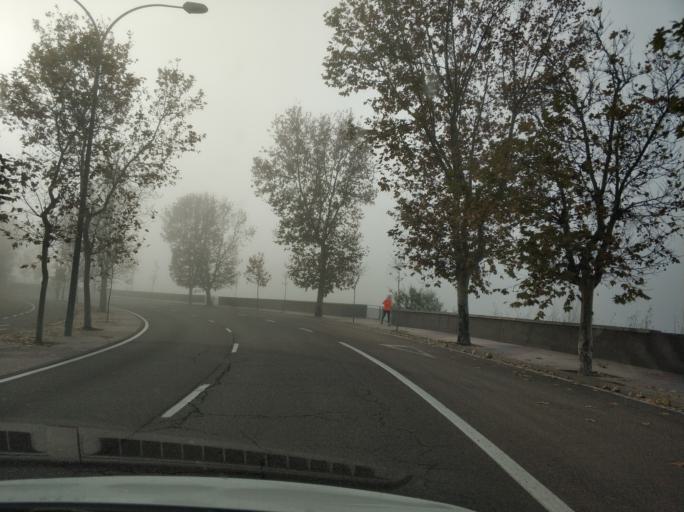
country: ES
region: Castille and Leon
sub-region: Provincia de Salamanca
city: Salamanca
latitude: 40.9617
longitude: -5.6750
